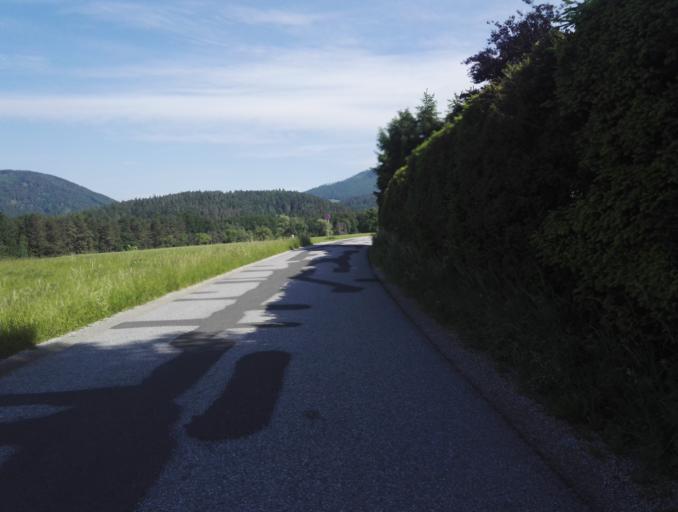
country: AT
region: Styria
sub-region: Politischer Bezirk Graz-Umgebung
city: Stattegg
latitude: 47.1452
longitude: 15.4339
